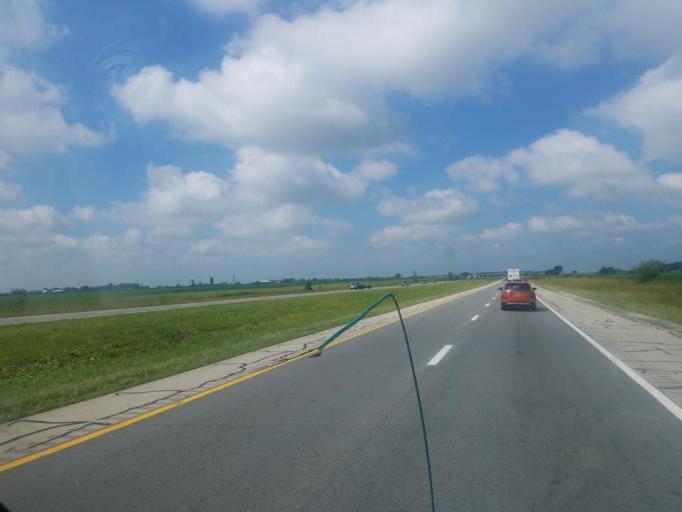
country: US
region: Ohio
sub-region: Madison County
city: Bethel
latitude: 39.7200
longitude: -83.4015
